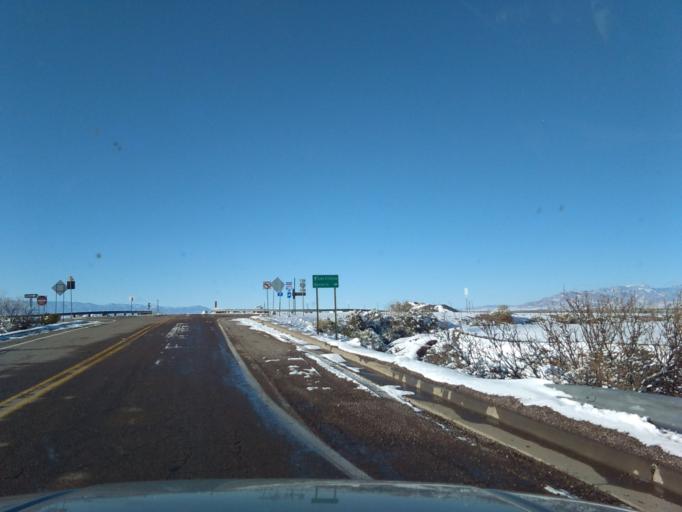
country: US
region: New Mexico
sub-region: Socorro County
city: Socorro
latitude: 33.6360
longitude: -107.1197
